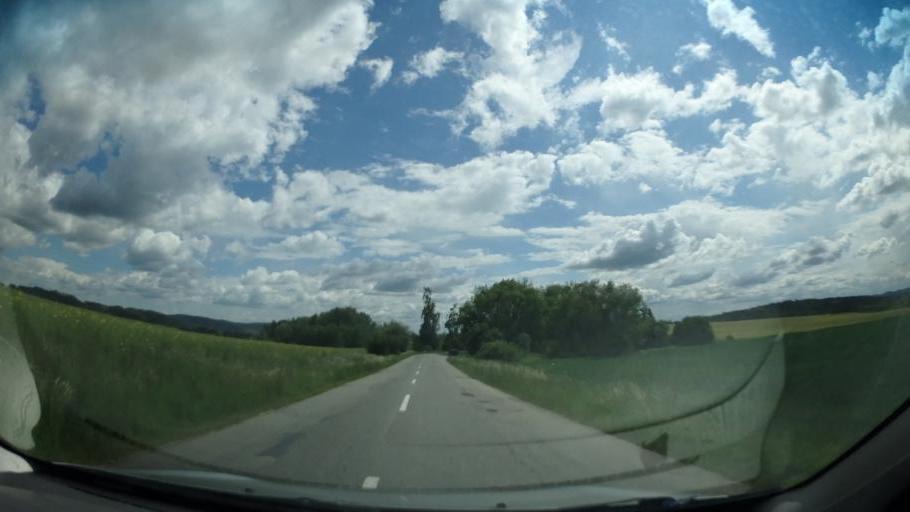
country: CZ
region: South Moravian
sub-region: Okres Blansko
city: Letovice
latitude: 49.5896
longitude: 16.5952
